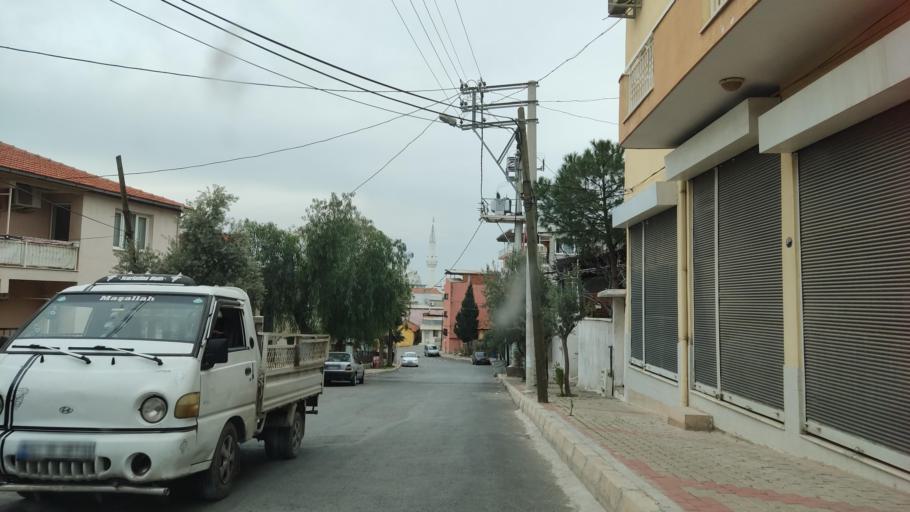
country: TR
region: Izmir
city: Karsiyaka
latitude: 38.4954
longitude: 27.0743
